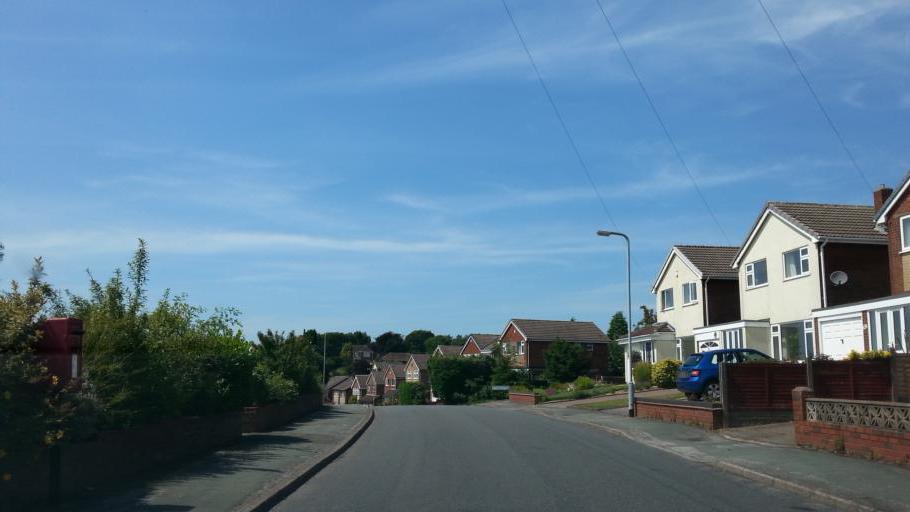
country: GB
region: England
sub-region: Staffordshire
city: Cannock
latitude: 52.7164
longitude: -2.0184
